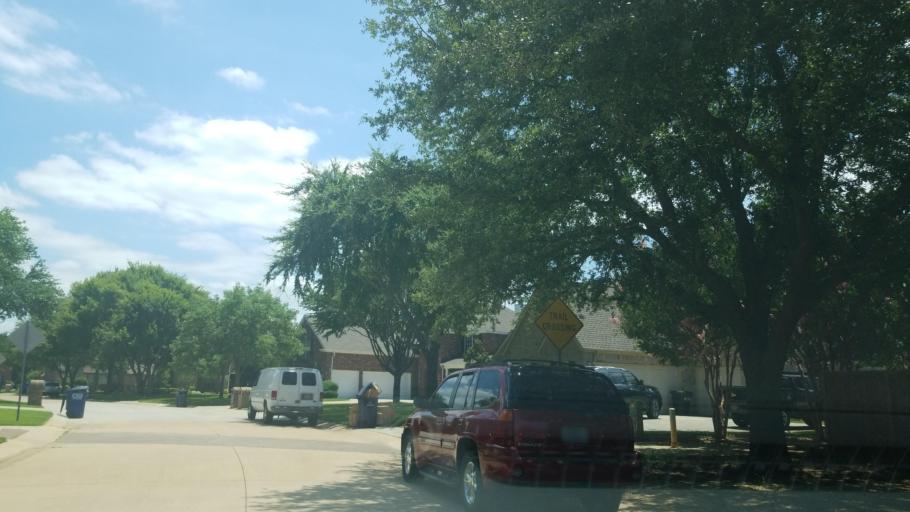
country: US
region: Texas
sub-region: Denton County
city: Copper Canyon
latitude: 33.0793
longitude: -97.0819
